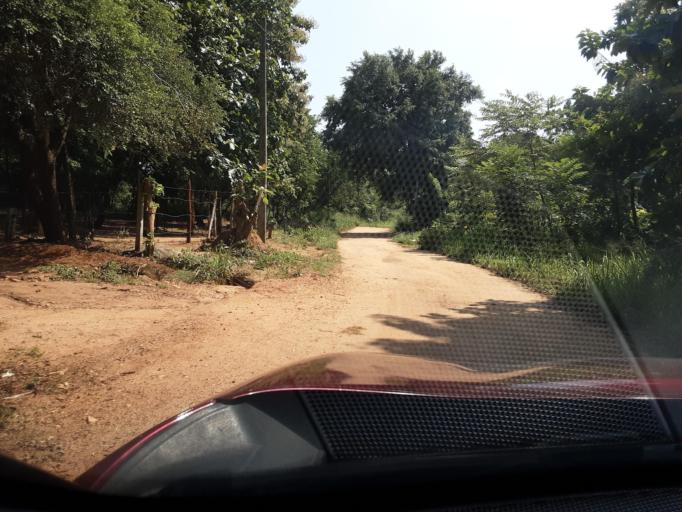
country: LK
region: Central
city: Sigiriya
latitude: 8.0042
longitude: 80.7469
